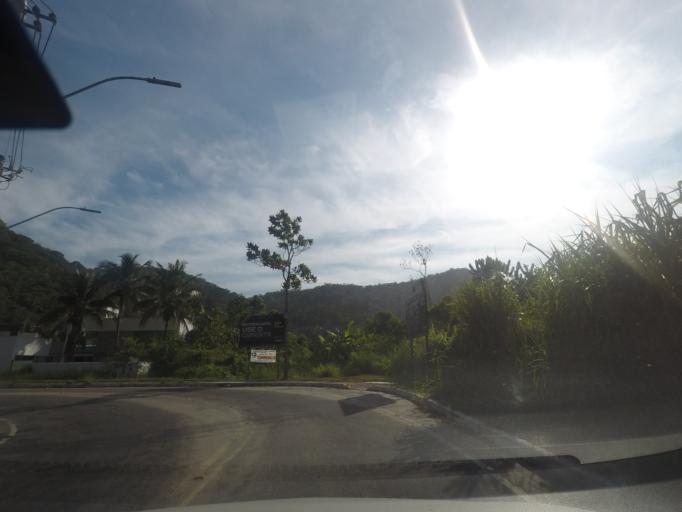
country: BR
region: Rio de Janeiro
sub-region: Niteroi
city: Niteroi
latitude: -22.9636
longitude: -43.0144
